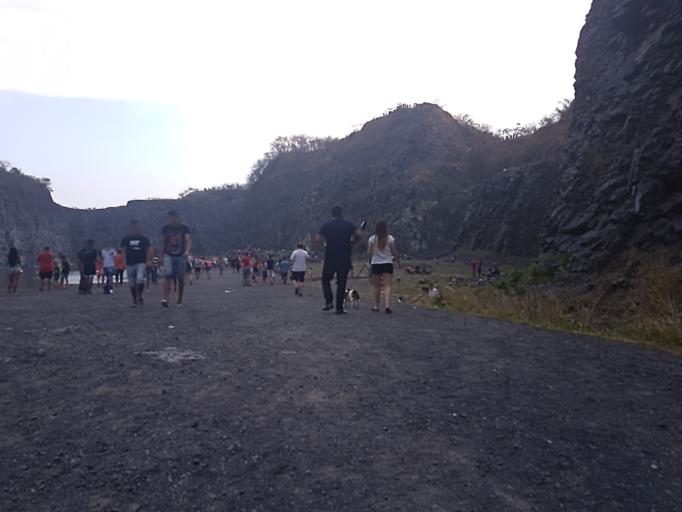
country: PY
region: Central
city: Nemby
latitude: -25.4030
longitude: -57.5361
